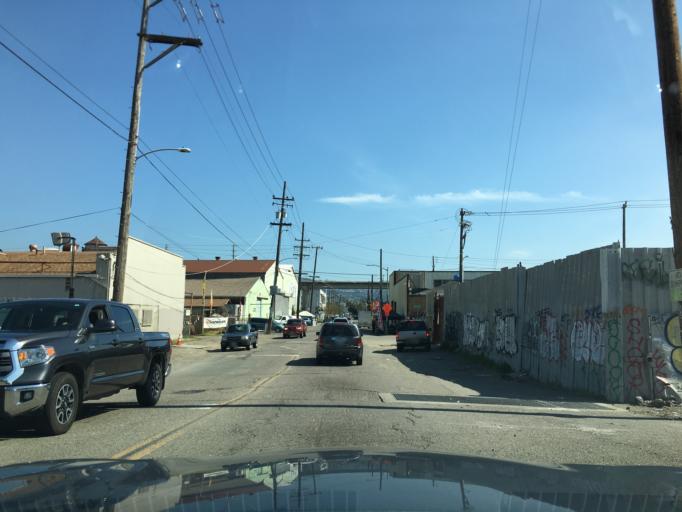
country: US
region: California
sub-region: Alameda County
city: Alameda
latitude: 37.7653
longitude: -122.2133
